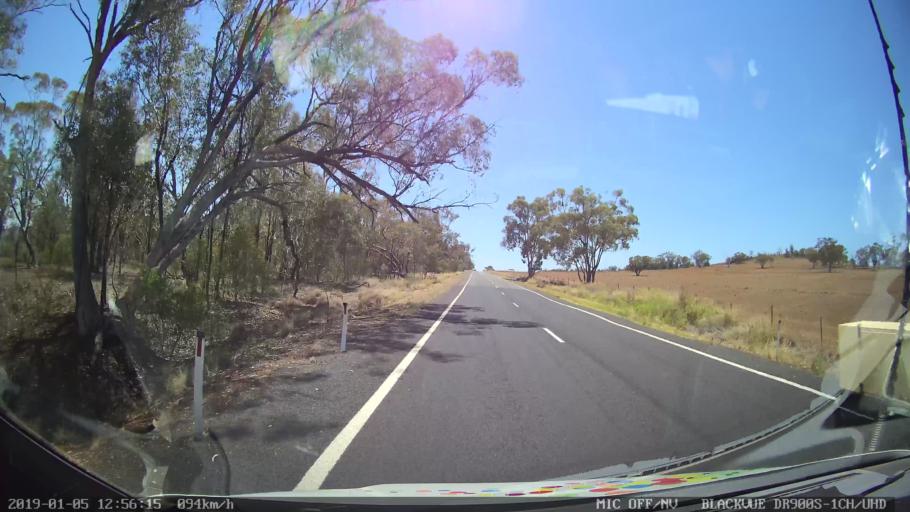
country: AU
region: New South Wales
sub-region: Warrumbungle Shire
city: Coonabarabran
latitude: -31.1157
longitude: 149.7177
